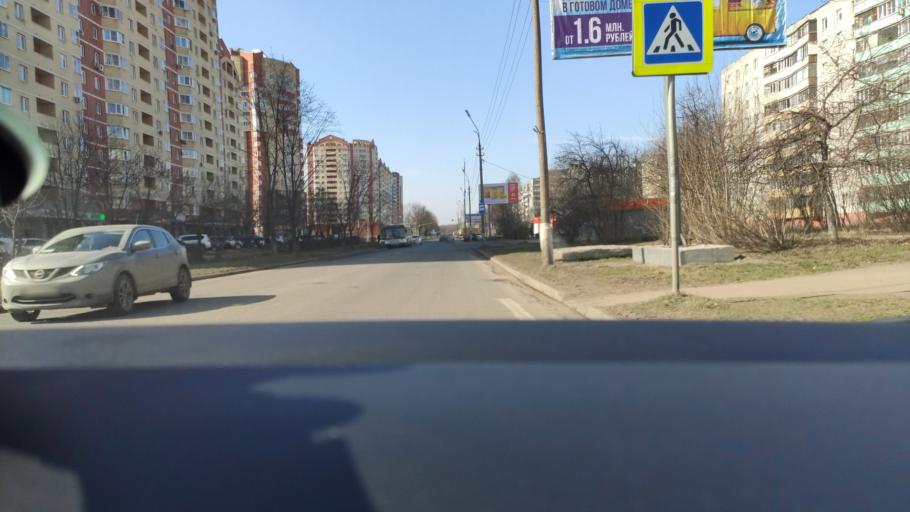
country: RU
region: Moskovskaya
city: Elektrostal'
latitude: 55.7692
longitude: 38.4323
